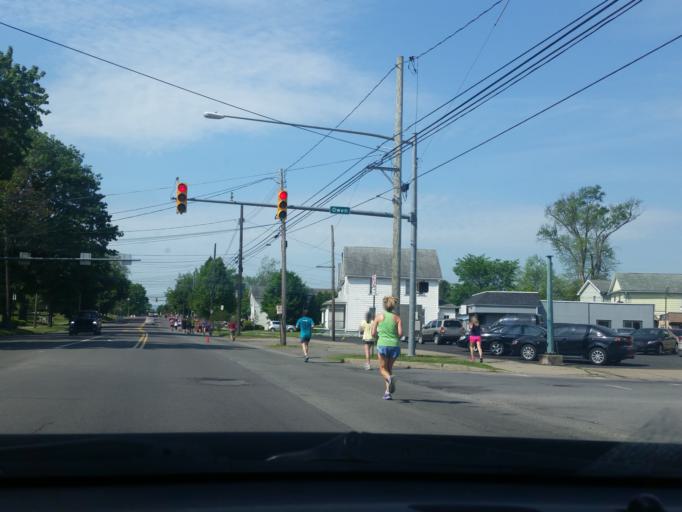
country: US
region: Pennsylvania
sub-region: Luzerne County
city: Swoyersville
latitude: 41.2947
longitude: -75.8653
